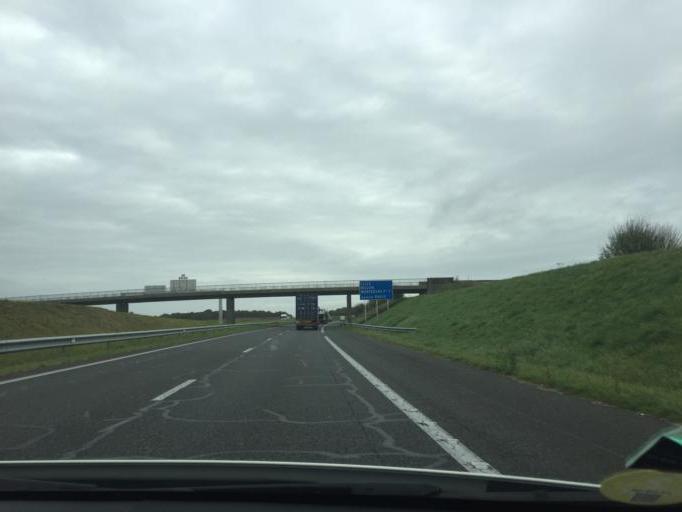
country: FR
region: Centre
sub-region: Departement du Loiret
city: Courtenay
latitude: 48.0649
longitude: 3.1097
